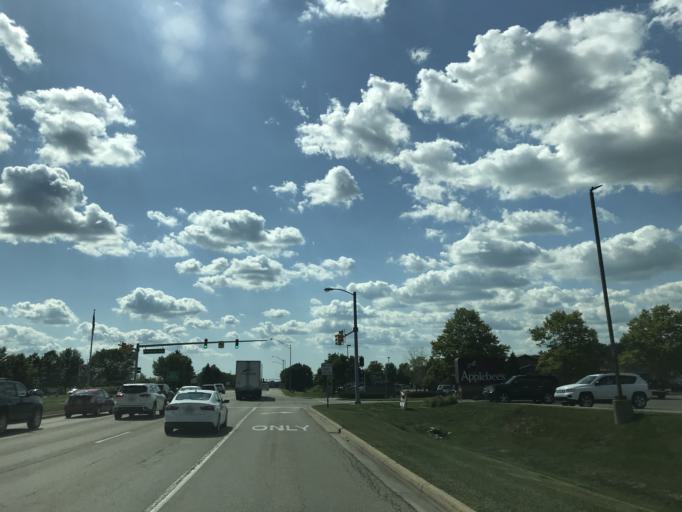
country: US
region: Michigan
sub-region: Kent County
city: Grandville
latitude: 42.8827
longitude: -85.7521
